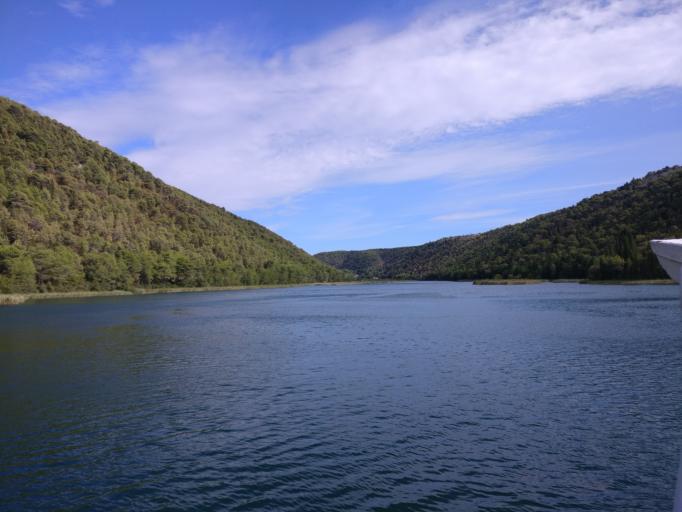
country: HR
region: Sibensko-Kniniska
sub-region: Grad Sibenik
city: Sibenik
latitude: 43.8209
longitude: 15.9463
